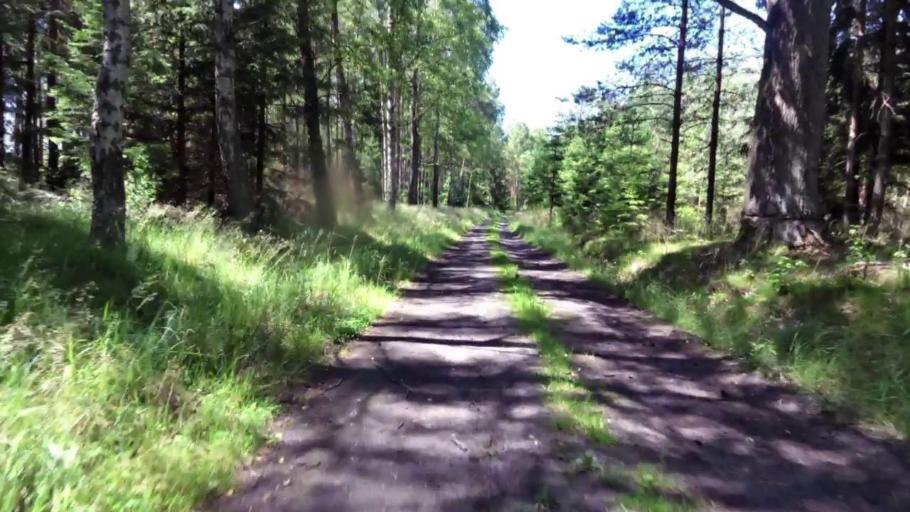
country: PL
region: West Pomeranian Voivodeship
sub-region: Powiat bialogardzki
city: Bialogard
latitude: 53.9524
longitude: 16.1082
